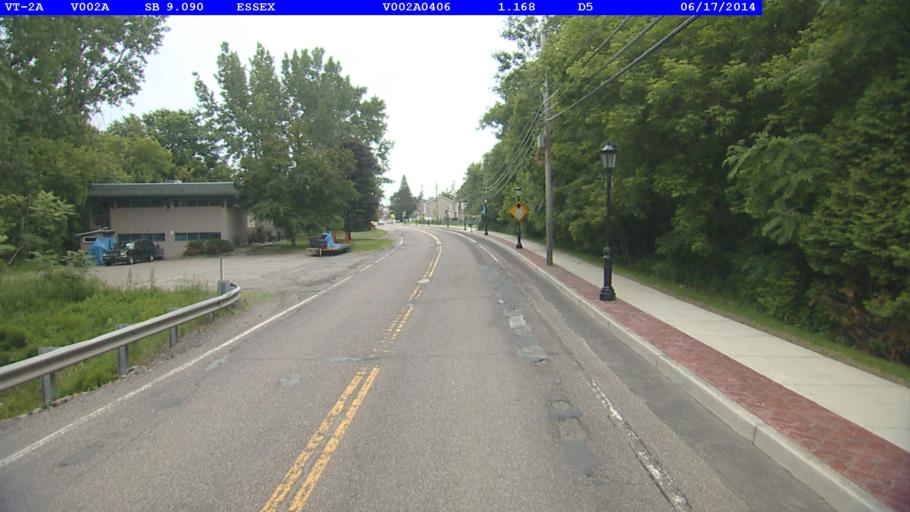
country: US
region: Vermont
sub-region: Chittenden County
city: Essex Junction
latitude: 44.4975
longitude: -73.1128
